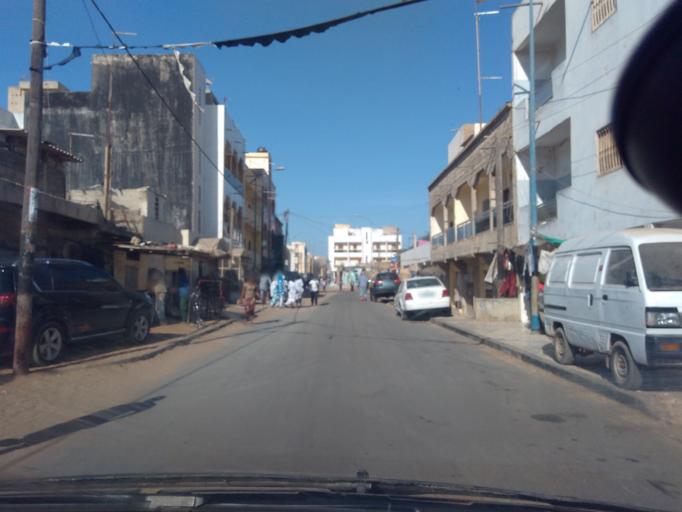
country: SN
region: Dakar
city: Pikine
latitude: 14.7565
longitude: -17.4325
